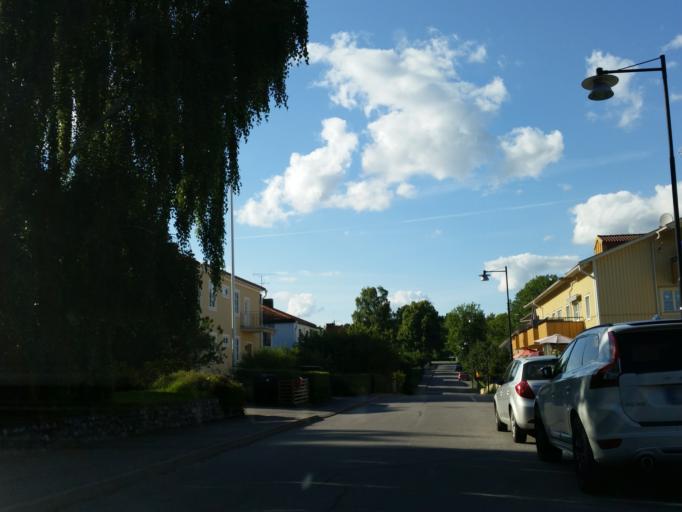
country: SE
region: Soedermanland
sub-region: Trosa Kommun
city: Trosa
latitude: 58.8960
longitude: 17.5454
